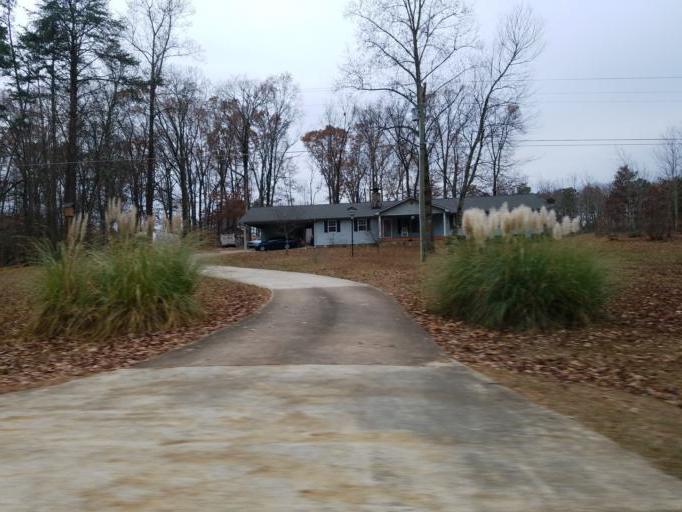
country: US
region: Georgia
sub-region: Dawson County
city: Dawsonville
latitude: 34.4426
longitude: -84.0964
